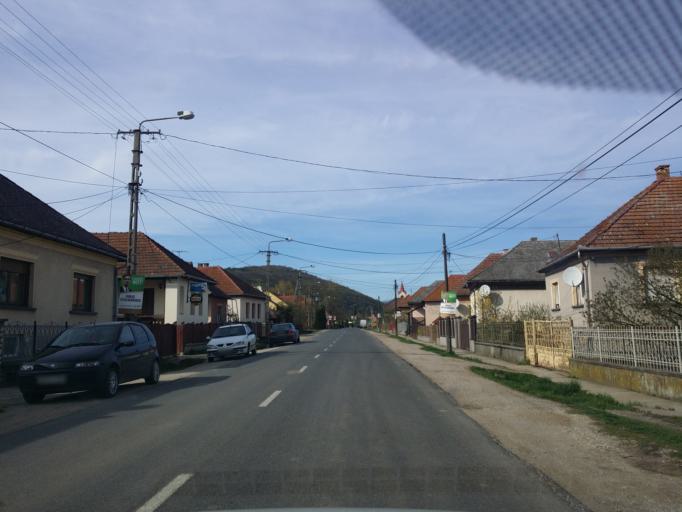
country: HU
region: Borsod-Abauj-Zemplen
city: Szendro
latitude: 48.4683
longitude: 20.6894
